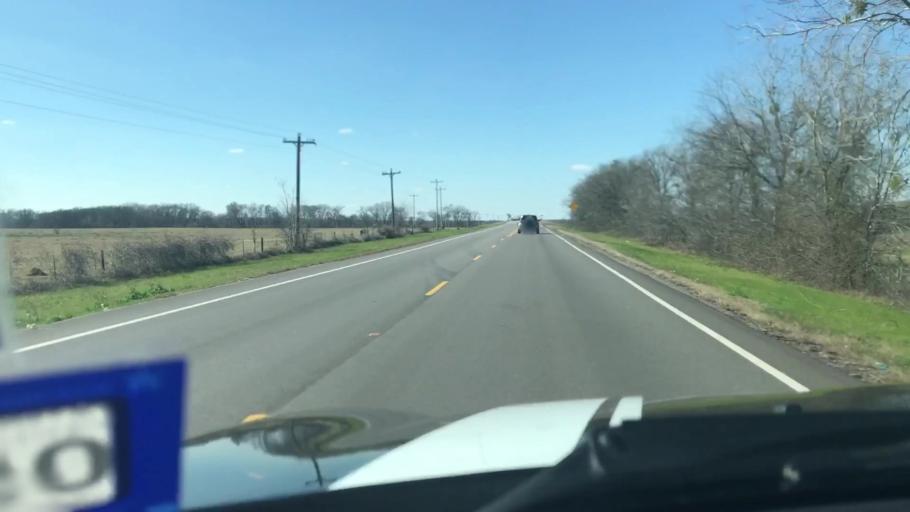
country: US
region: Texas
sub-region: Robertson County
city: Hearne
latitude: 30.8814
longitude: -96.6345
